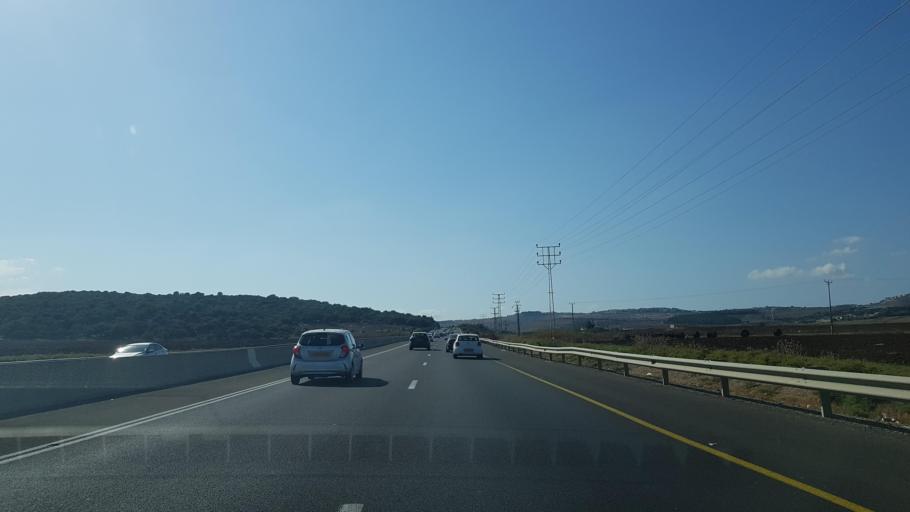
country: IL
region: Northern District
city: Rumat Heib
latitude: 32.7727
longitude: 35.2716
